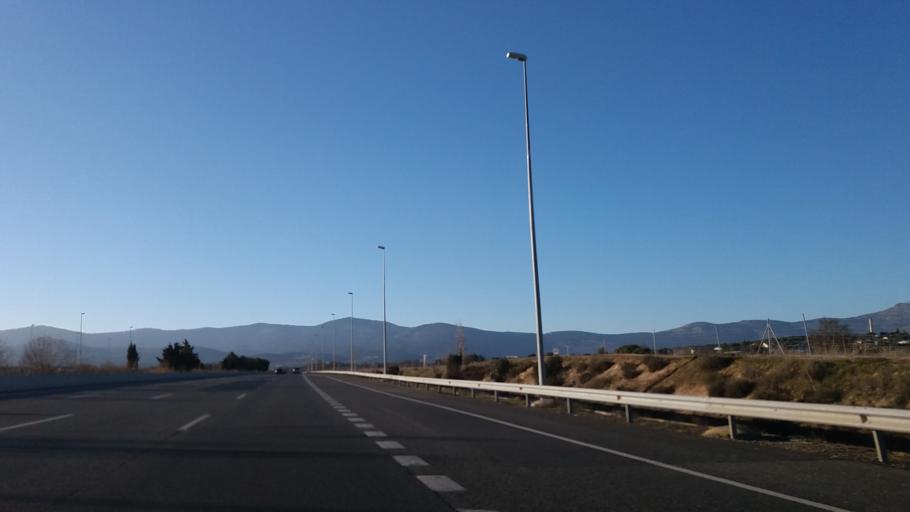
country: ES
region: Madrid
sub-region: Provincia de Madrid
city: Alpedrete
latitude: 40.6442
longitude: -4.0438
